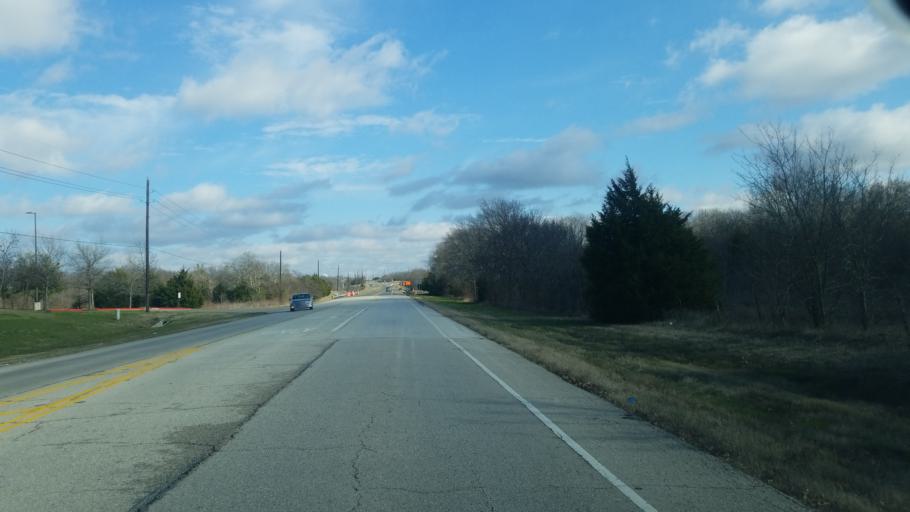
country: US
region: Texas
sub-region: Rockwall County
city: Rockwall
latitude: 32.9070
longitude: -96.4457
